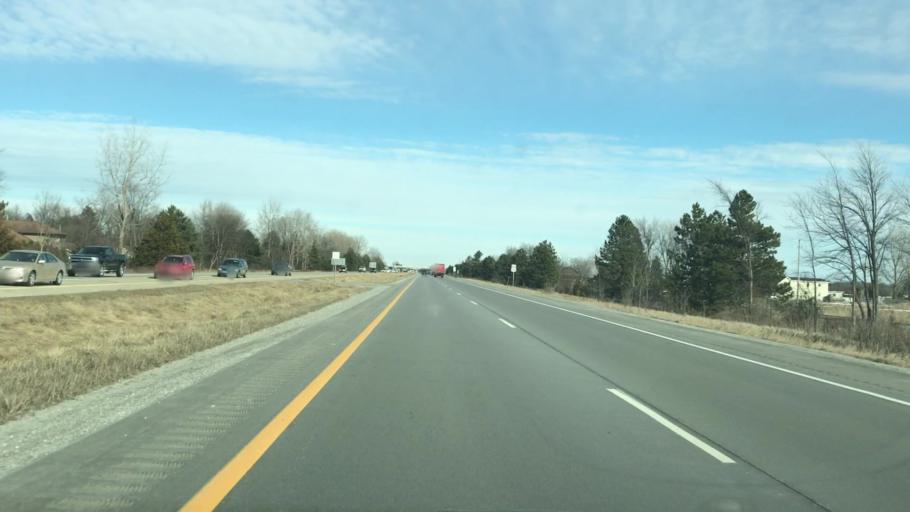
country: US
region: Michigan
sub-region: Bay County
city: Auburn
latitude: 43.5968
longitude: -84.0825
